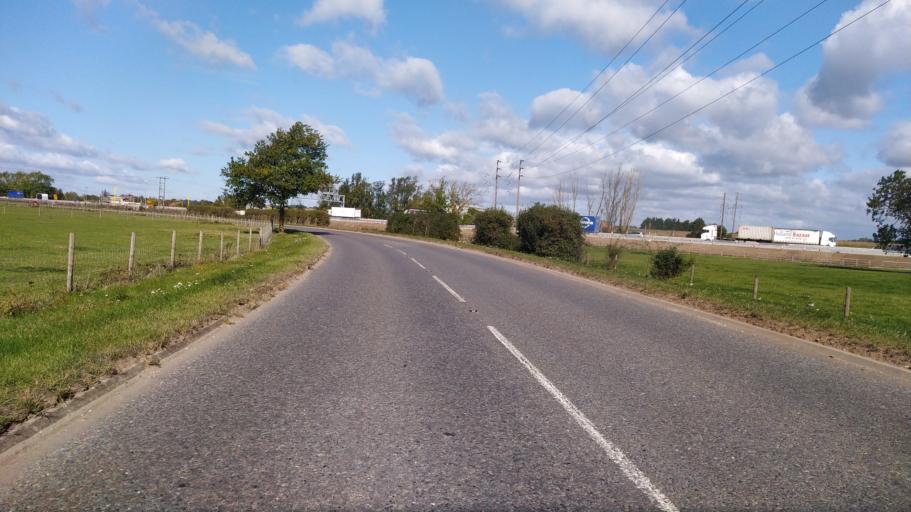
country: GB
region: England
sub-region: West Berkshire
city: Calcot
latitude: 51.4199
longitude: -1.0192
